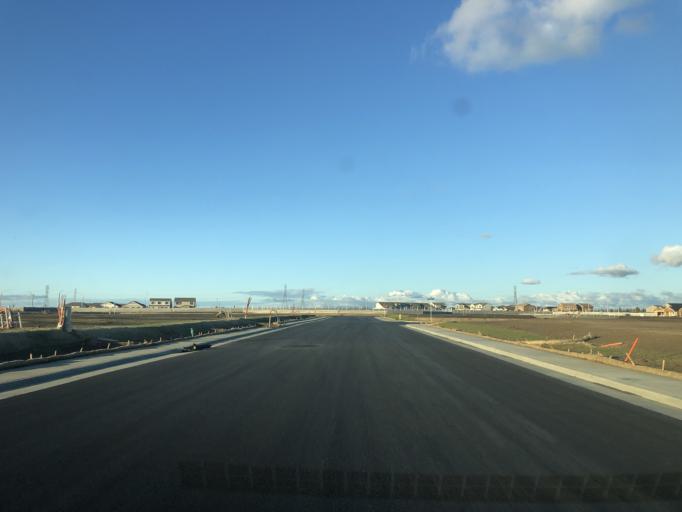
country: US
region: California
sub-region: Sacramento County
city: Antelope
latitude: 38.7564
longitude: -121.3661
